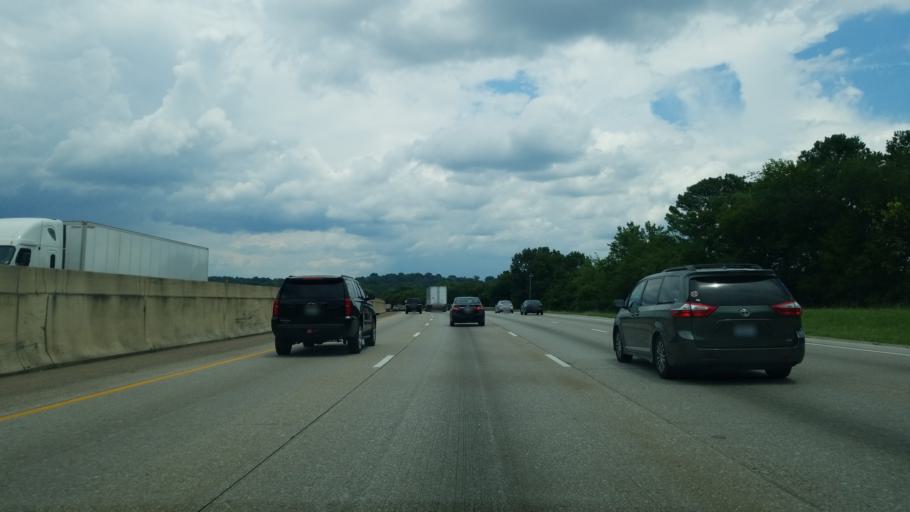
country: US
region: Tennessee
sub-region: Hamilton County
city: East Brainerd
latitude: 35.0127
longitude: -85.1842
